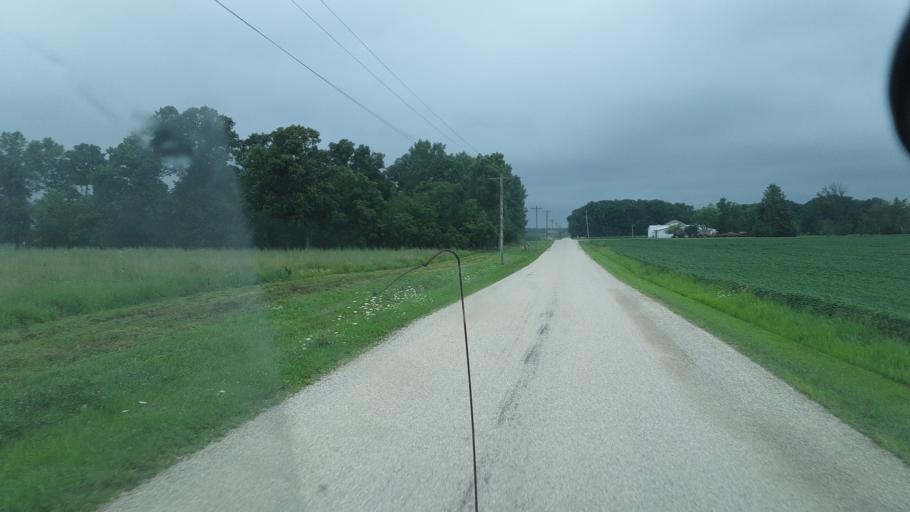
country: US
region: Indiana
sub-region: Adams County
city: Berne
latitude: 40.6420
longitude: -85.0022
